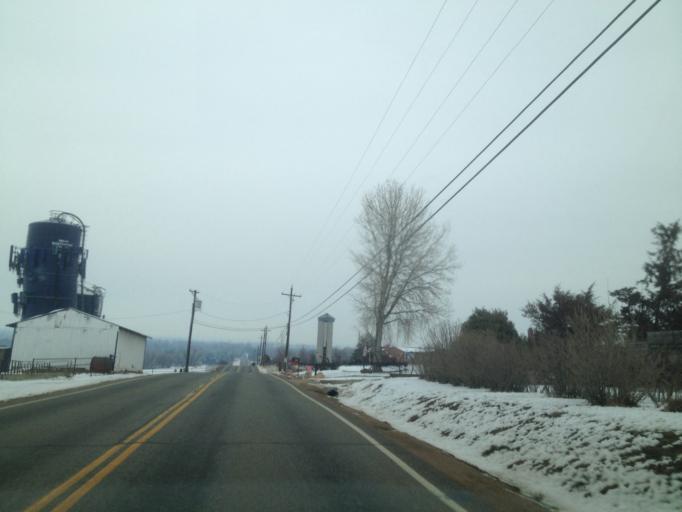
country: US
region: Colorado
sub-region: Boulder County
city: Gunbarrel
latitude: 40.0831
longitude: -105.1691
